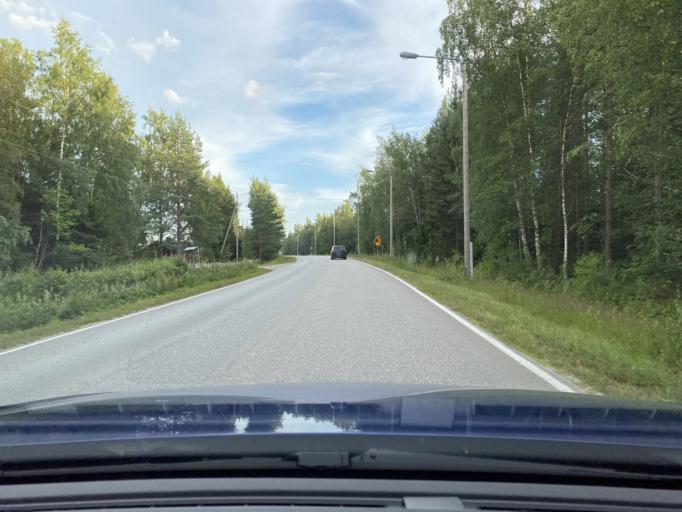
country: FI
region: Ostrobothnia
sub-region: Vaasa
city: Korsnaes
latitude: 62.9465
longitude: 21.1757
